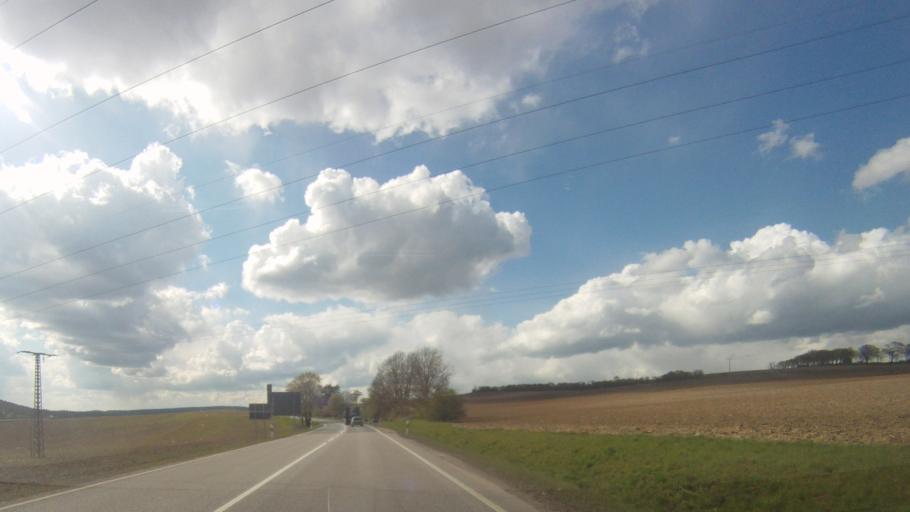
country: DE
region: Thuringia
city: Eisfeld
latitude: 50.4327
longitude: 10.8962
